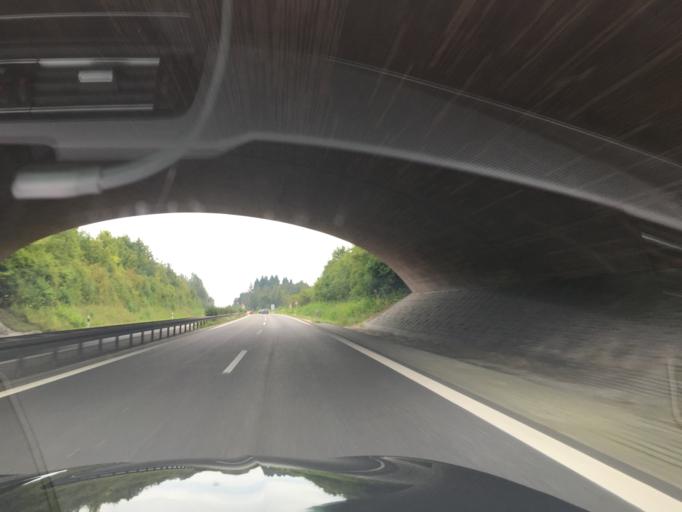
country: DE
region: Baden-Wuerttemberg
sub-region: Freiburg Region
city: Radolfzell am Bodensee
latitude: 47.7388
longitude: 9.0187
